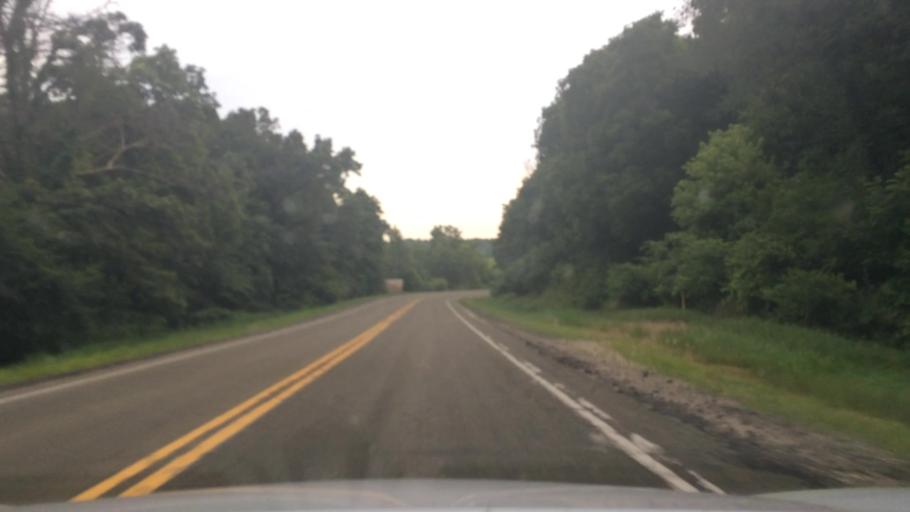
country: US
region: Wisconsin
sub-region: Columbia County
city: Lodi
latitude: 43.3207
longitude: -89.5032
